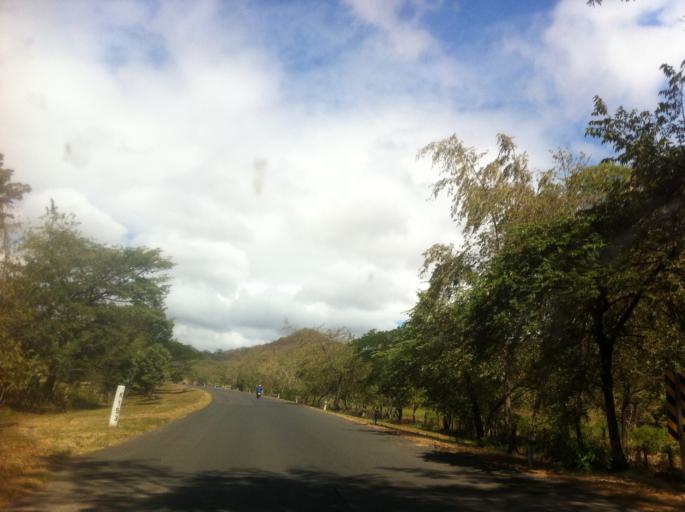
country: NI
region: Chontales
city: Juigalpa
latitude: 12.0393
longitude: -85.2685
